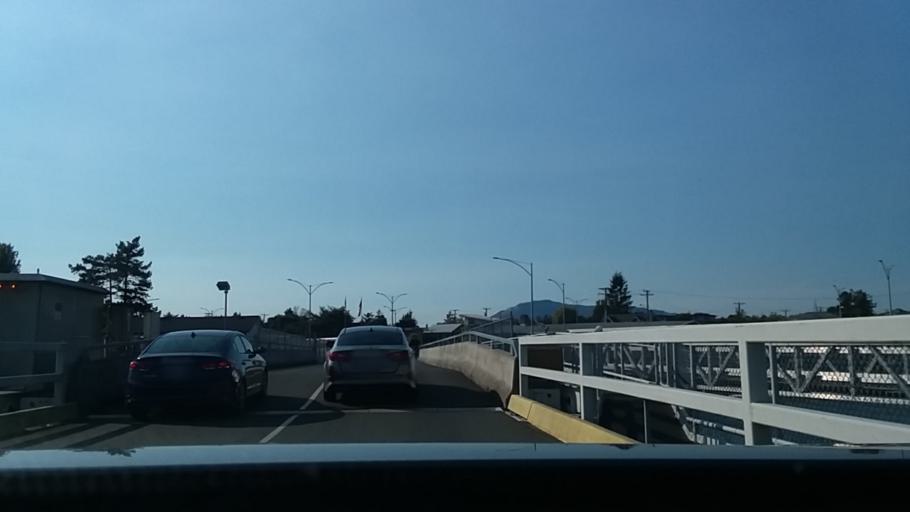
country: CA
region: British Columbia
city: North Saanich
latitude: 48.6433
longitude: -123.3968
